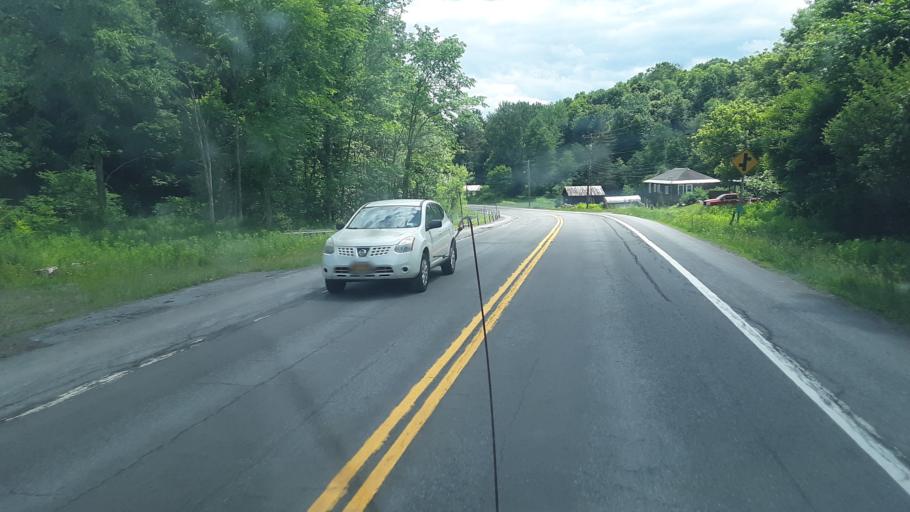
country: US
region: New York
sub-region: Oneida County
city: Rome
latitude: 43.3750
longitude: -75.4842
